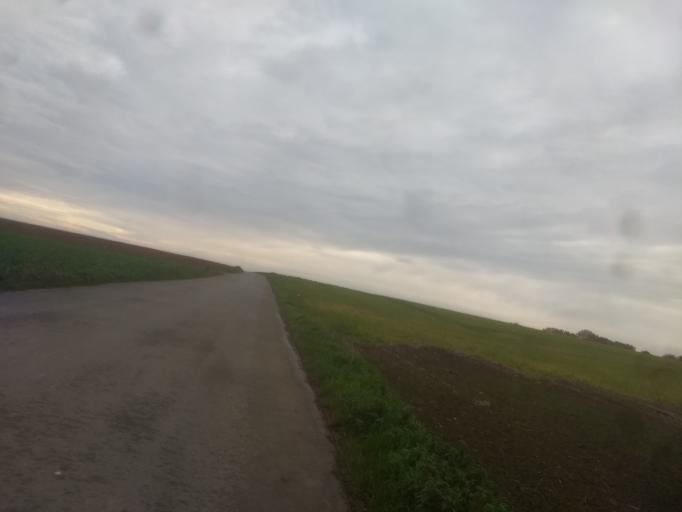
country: FR
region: Nord-Pas-de-Calais
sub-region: Departement du Pas-de-Calais
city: Dainville
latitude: 50.2554
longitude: 2.7202
